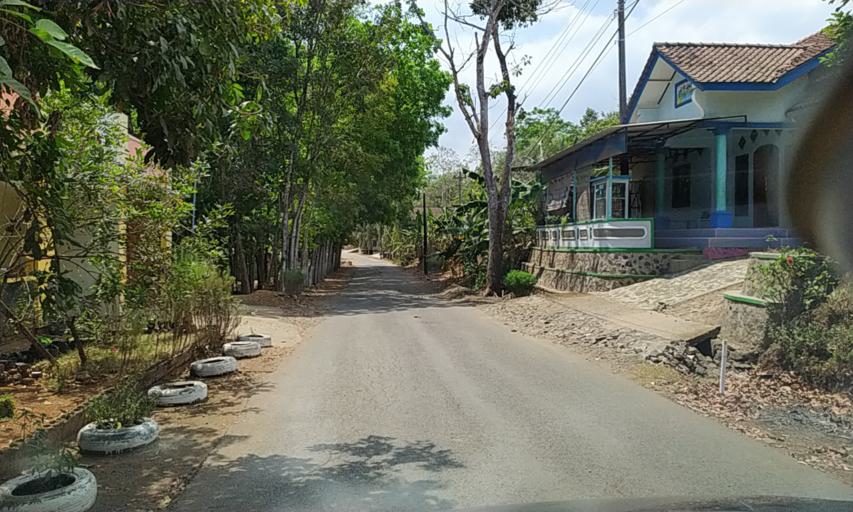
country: ID
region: Central Java
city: Karanganyar
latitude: -7.3238
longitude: 108.6473
